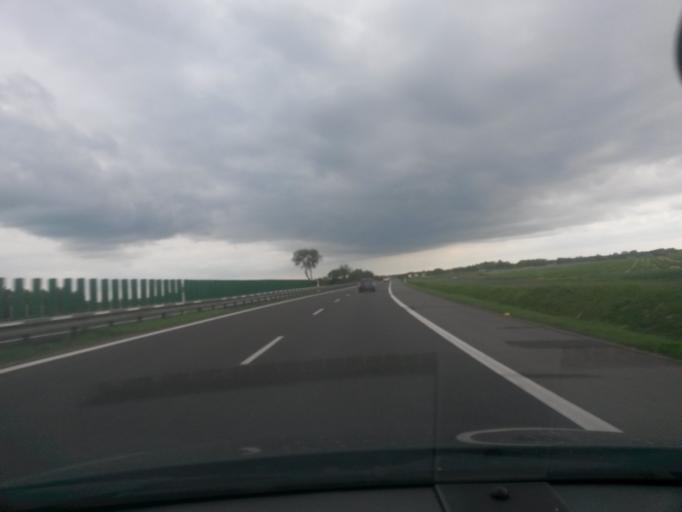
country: PL
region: Masovian Voivodeship
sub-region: Powiat plonski
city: Zaluski
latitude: 52.5771
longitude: 20.4803
